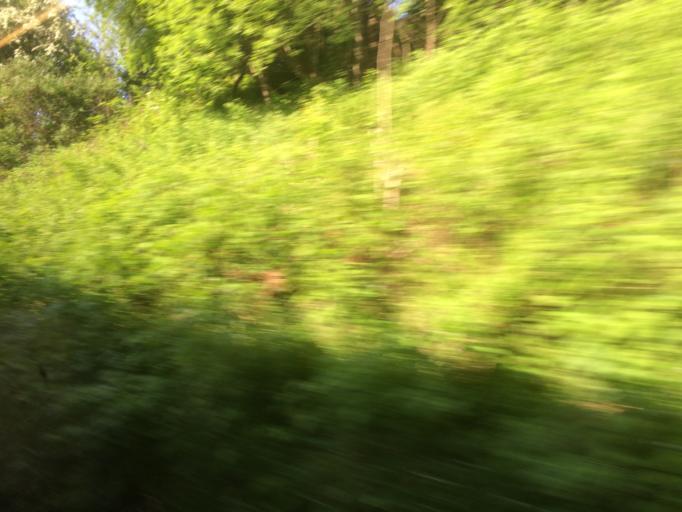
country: GB
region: Scotland
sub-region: Perth and Kinross
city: Perth
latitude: 56.3771
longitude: -3.4291
